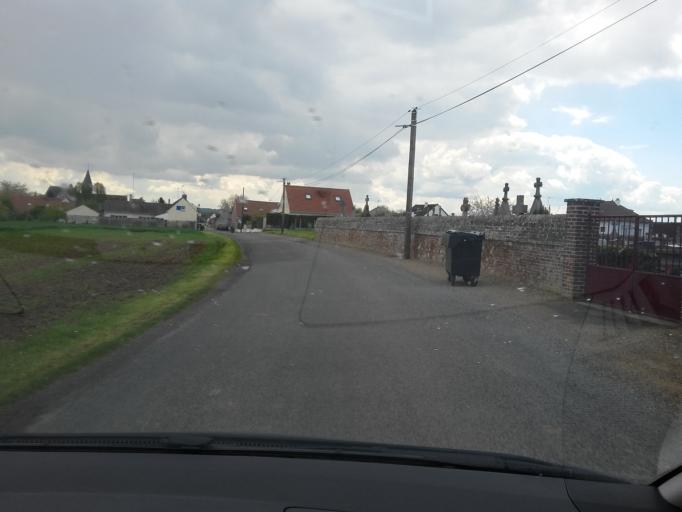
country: FR
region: Picardie
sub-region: Departement de l'Oise
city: Chevrieres
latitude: 49.3501
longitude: 2.6807
